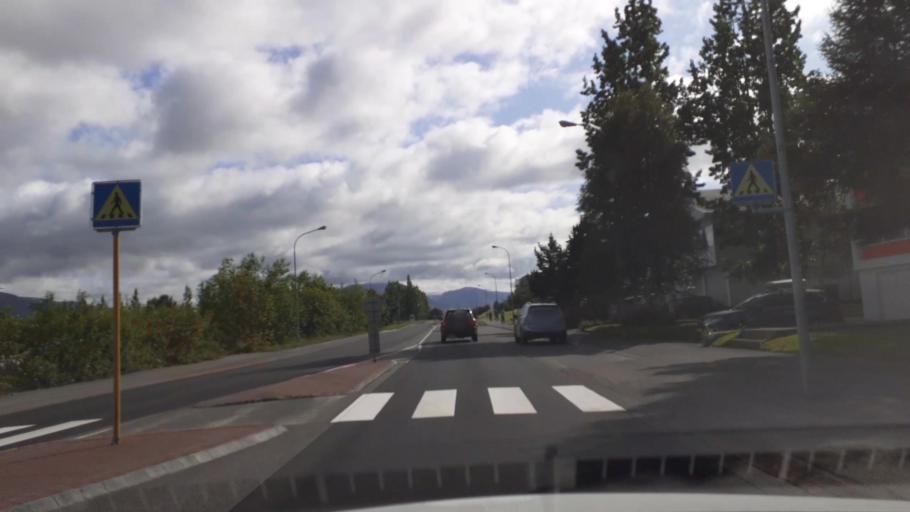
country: IS
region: Northeast
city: Akureyri
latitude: 65.6758
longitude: -18.0979
